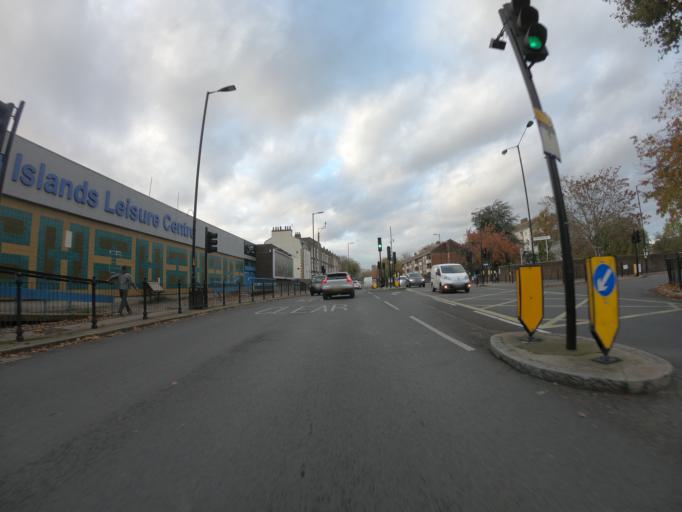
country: GB
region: England
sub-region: Greater London
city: Bethnal Green
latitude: 51.4962
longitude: -0.0523
